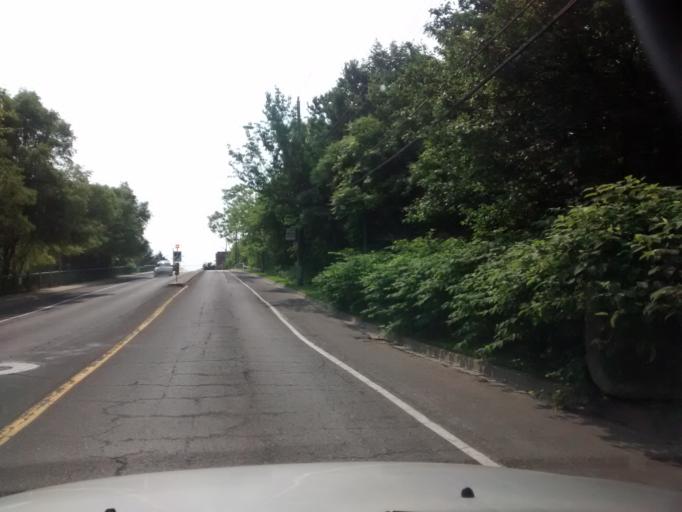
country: CA
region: Ontario
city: Hamilton
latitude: 43.2317
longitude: -79.8154
